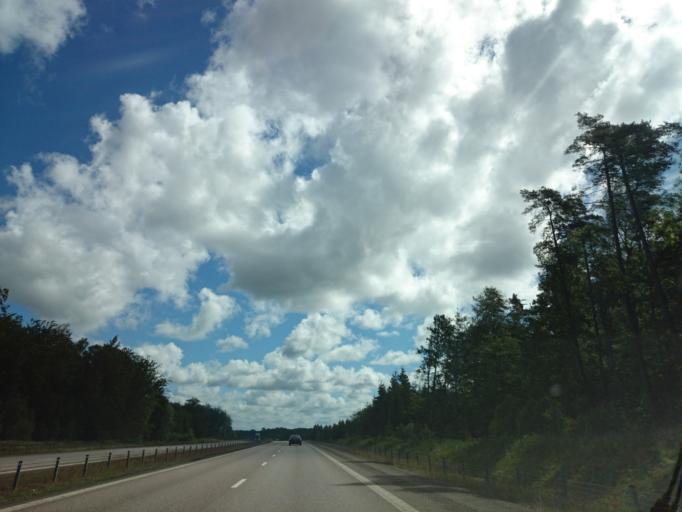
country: SE
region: Skane
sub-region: Orkelljunga Kommun
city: OErkelljunga
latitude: 56.2619
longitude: 13.2999
